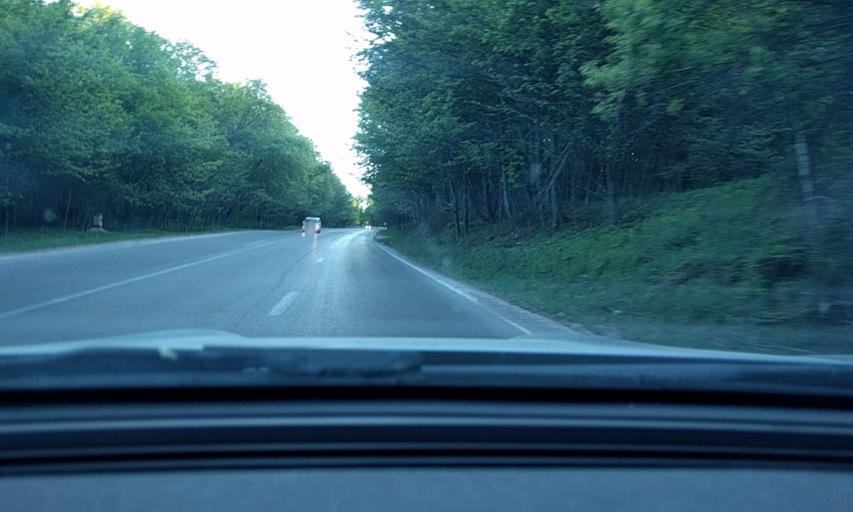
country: RO
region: Covasna
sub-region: Comuna Bretcu
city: Bretcu
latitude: 46.0662
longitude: 26.3729
